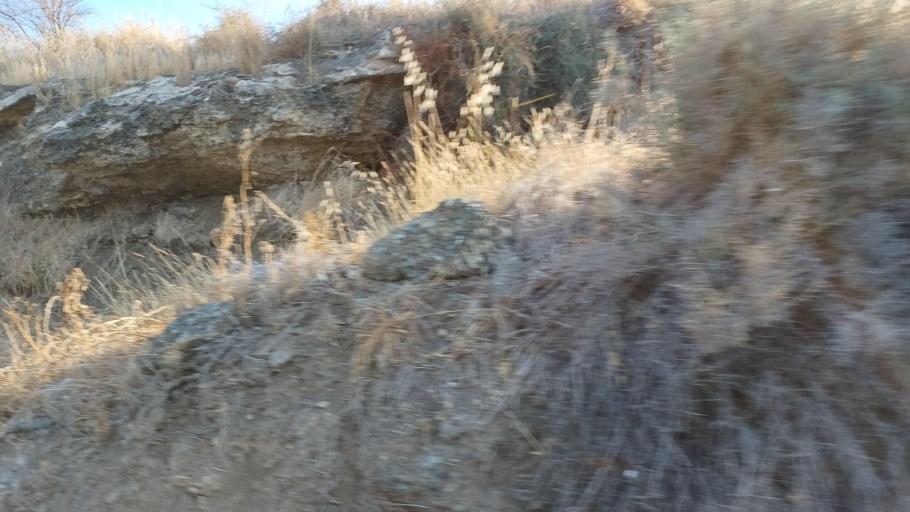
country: CY
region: Pafos
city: Polis
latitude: 35.0592
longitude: 32.4656
